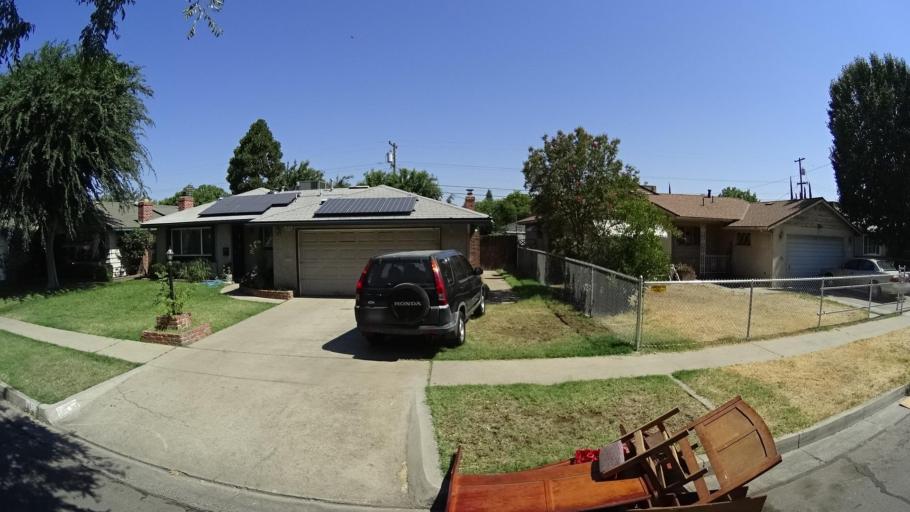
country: US
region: California
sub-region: Fresno County
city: Fresno
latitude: 36.7905
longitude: -119.7787
